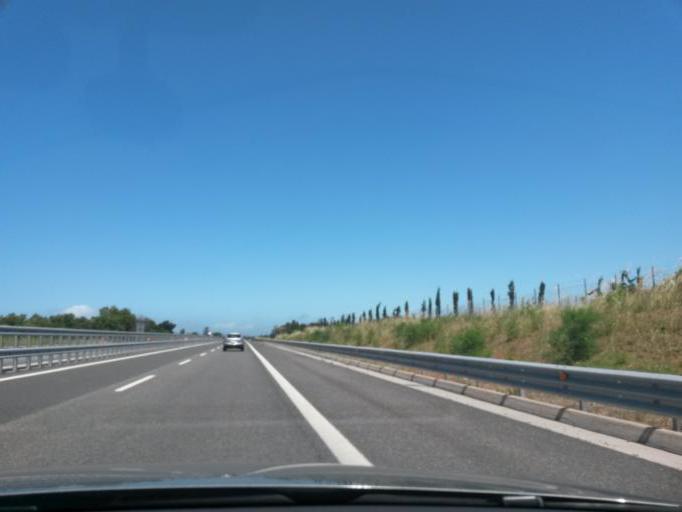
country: IT
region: Tuscany
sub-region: Provincia di Livorno
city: S.P. in Palazzi
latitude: 43.3453
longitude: 10.5185
